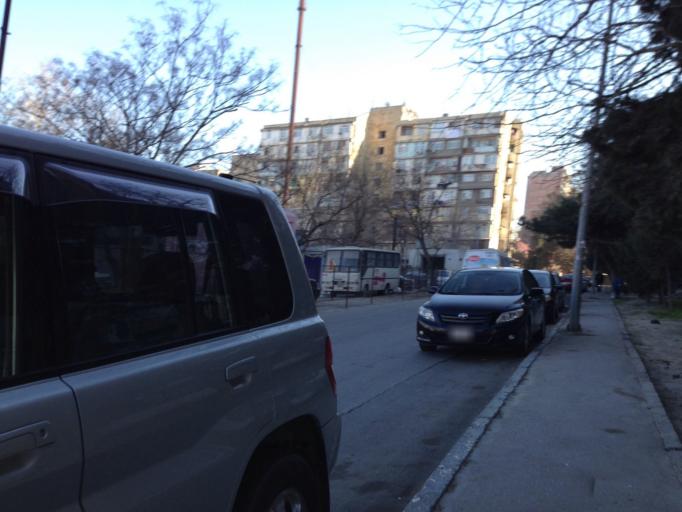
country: AZ
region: Baki
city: Baku
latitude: 40.3925
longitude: 49.8745
